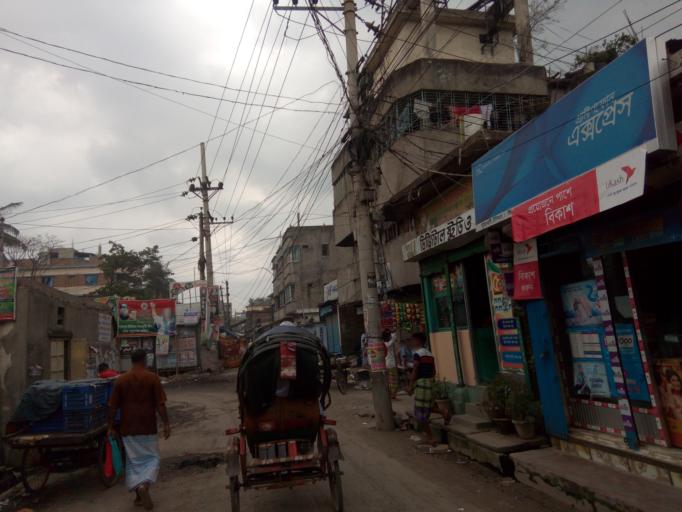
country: BD
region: Dhaka
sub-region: Dhaka
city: Dhaka
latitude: 23.6855
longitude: 90.4434
